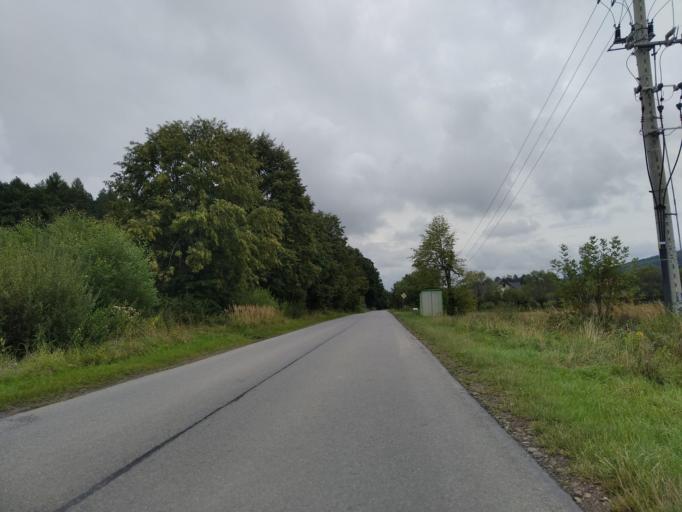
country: PL
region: Subcarpathian Voivodeship
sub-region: Powiat przemyski
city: Bircza
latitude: 49.6884
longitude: 22.3965
